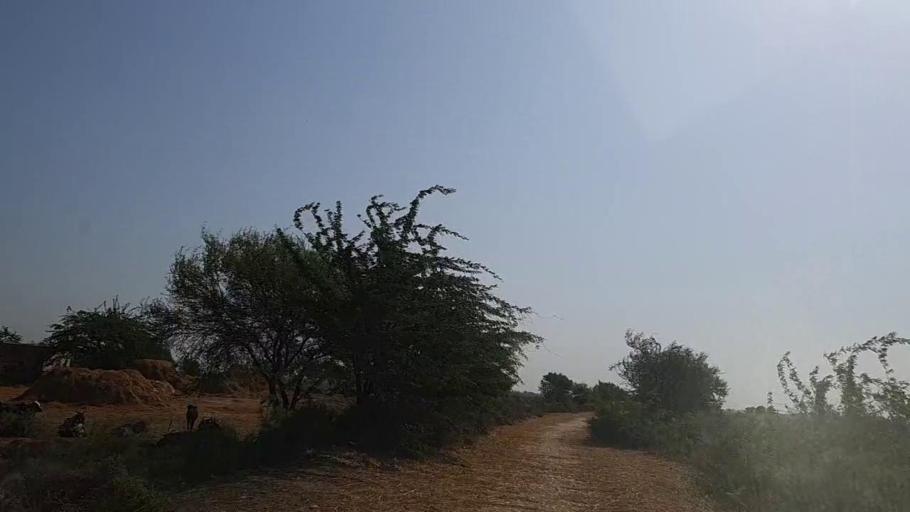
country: PK
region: Sindh
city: Daro Mehar
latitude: 24.7183
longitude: 68.1161
